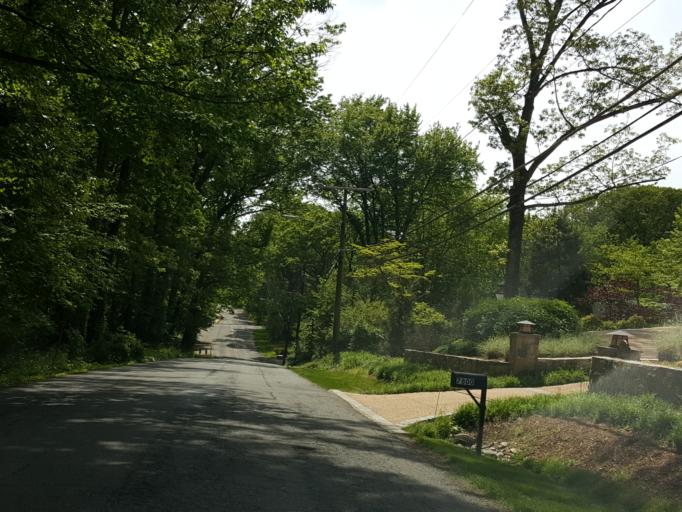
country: US
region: Virginia
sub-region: Fairfax County
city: Annandale
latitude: 38.8455
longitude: -77.2109
